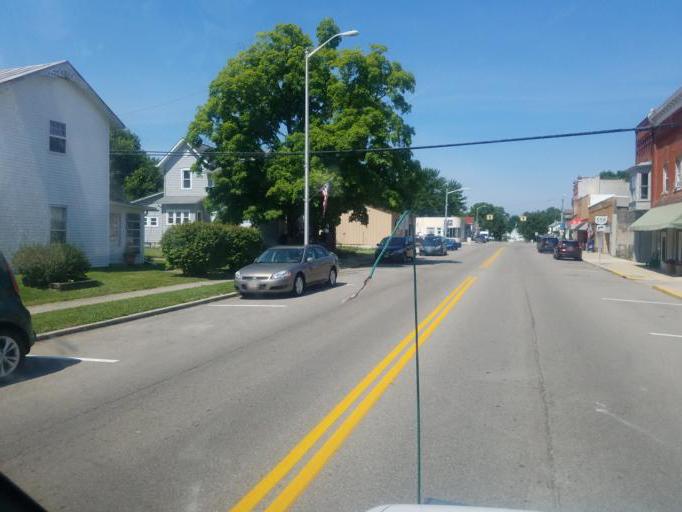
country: US
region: Ohio
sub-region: Champaign County
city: North Lewisburg
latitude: 40.2230
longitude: -83.5555
